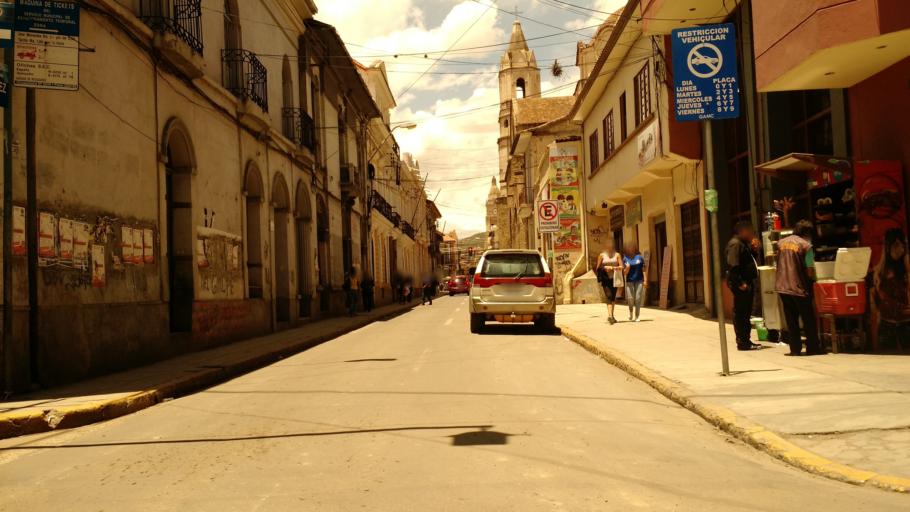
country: BO
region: Cochabamba
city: Cochabamba
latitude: -17.3948
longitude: -66.1596
